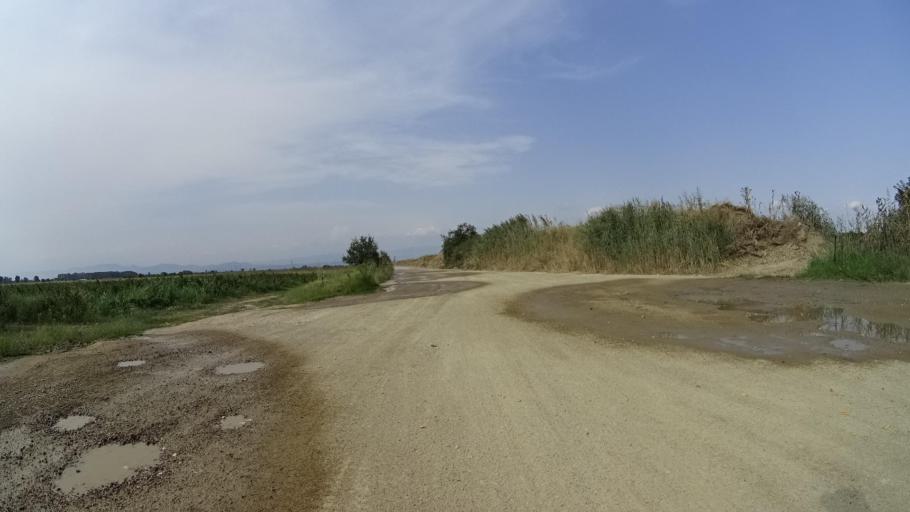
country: BG
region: Plovdiv
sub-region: Obshtina Kaloyanovo
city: Kaloyanovo
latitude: 42.3062
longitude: 24.7994
